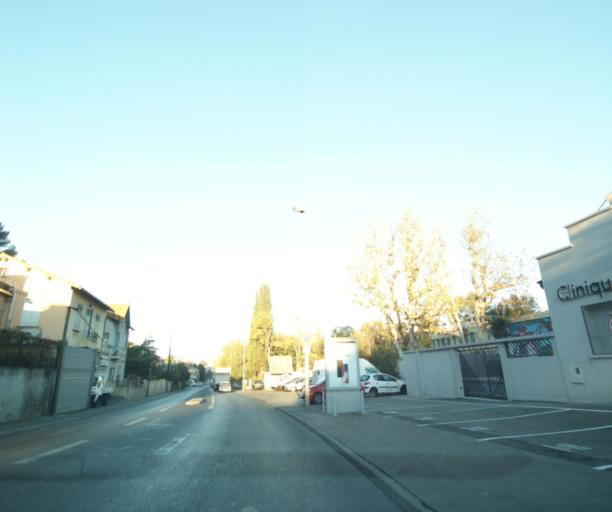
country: FR
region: Provence-Alpes-Cote d'Azur
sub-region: Departement des Bouches-du-Rhone
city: Marseille 12
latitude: 43.3257
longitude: 5.4411
